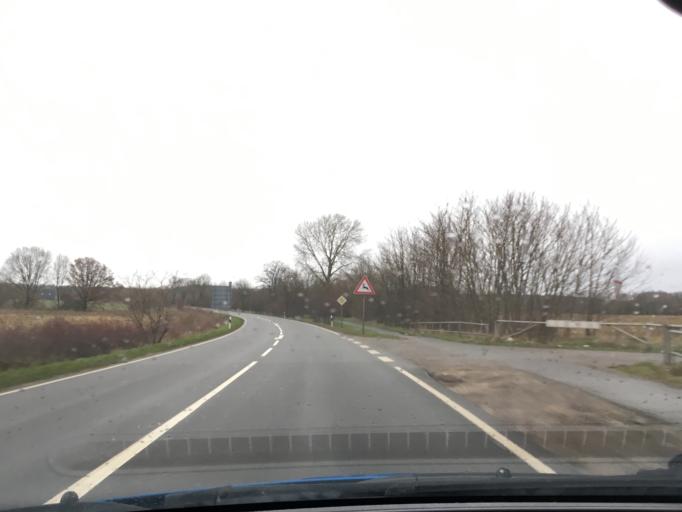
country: DE
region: Schleswig-Holstein
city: Hornbek
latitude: 53.5540
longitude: 10.6485
